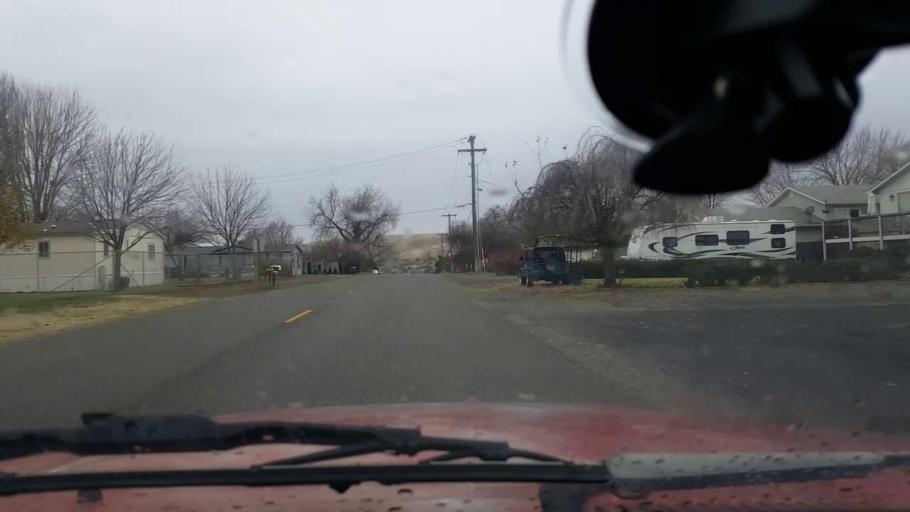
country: US
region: Washington
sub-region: Asotin County
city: Clarkston Heights-Vineland
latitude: 46.3822
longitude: -117.0856
